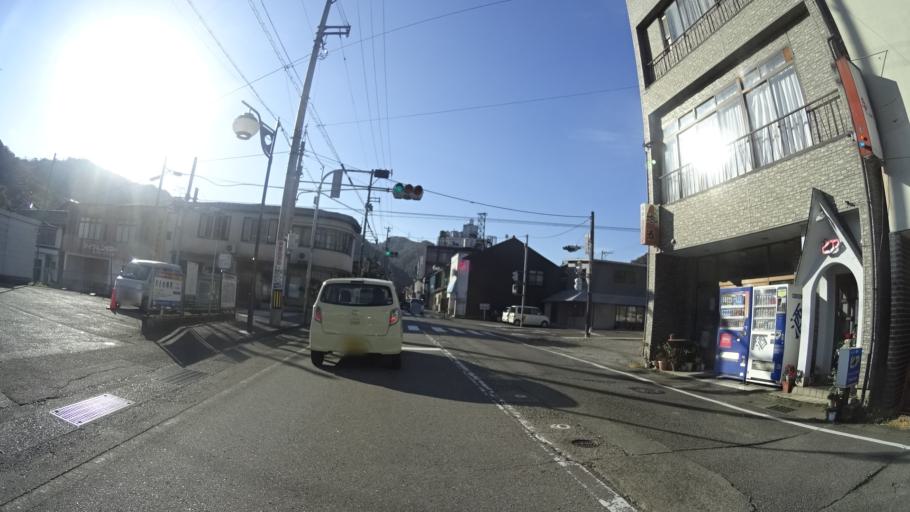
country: JP
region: Fukui
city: Maruoka
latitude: 36.2500
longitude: 136.3745
